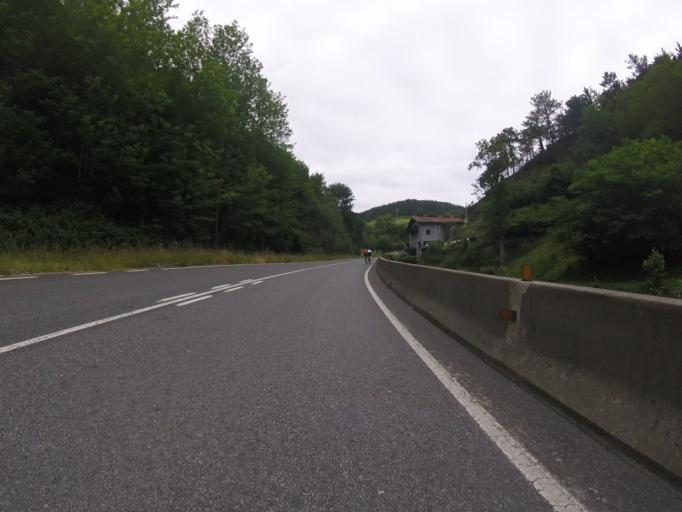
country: ES
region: Basque Country
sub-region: Provincia de Guipuzcoa
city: Orio
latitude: 43.2795
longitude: -2.1143
